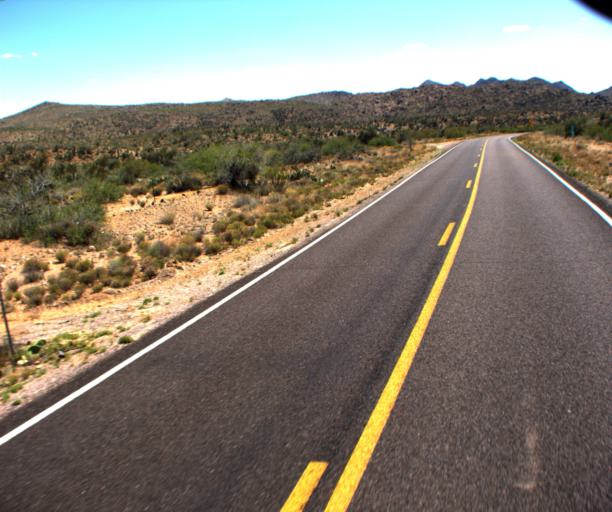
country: US
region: Arizona
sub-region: Yavapai County
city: Bagdad
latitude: 34.4938
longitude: -113.1775
